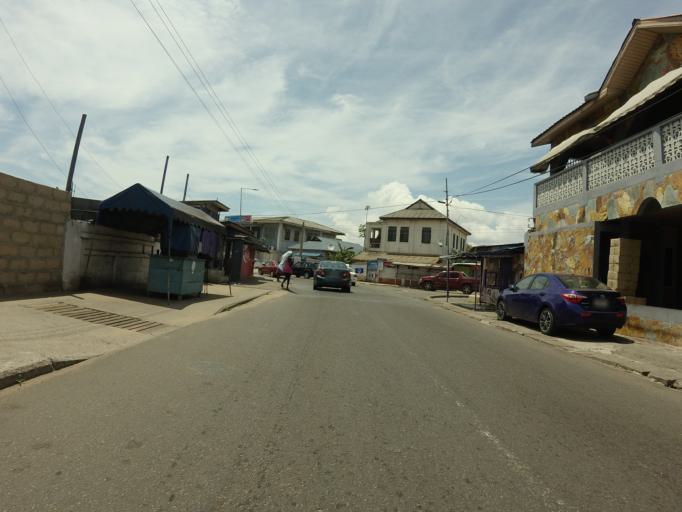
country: GH
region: Greater Accra
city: Accra
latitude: 5.5573
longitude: -0.2157
